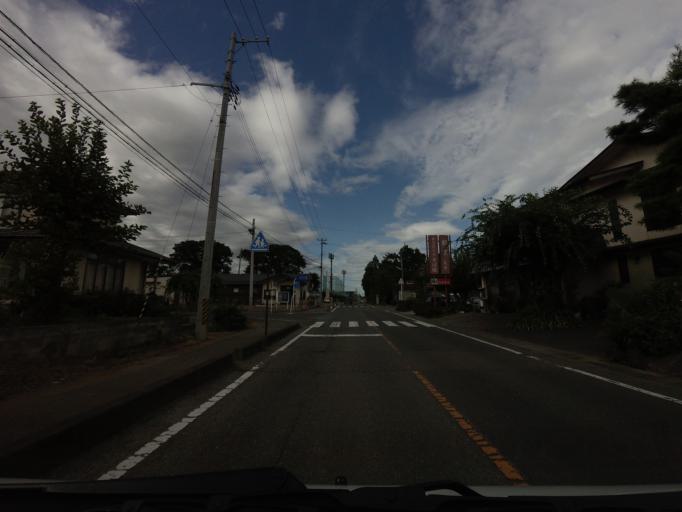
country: JP
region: Fukushima
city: Motomiya
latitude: 37.5349
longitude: 140.3718
